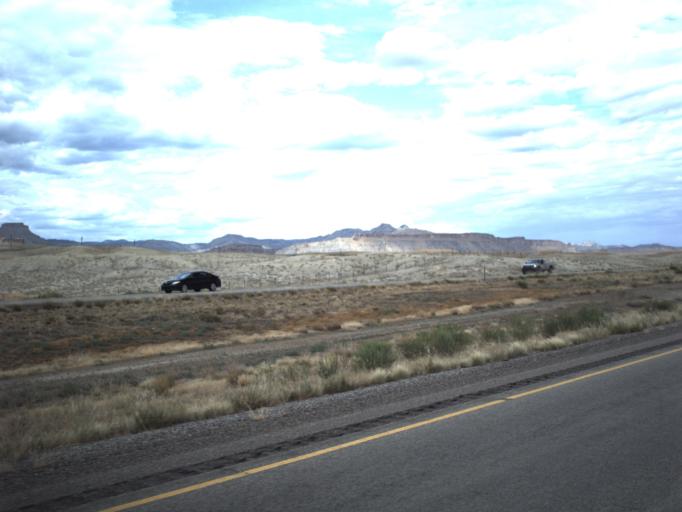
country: US
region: Utah
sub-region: Grand County
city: Moab
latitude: 38.9328
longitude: -109.8580
